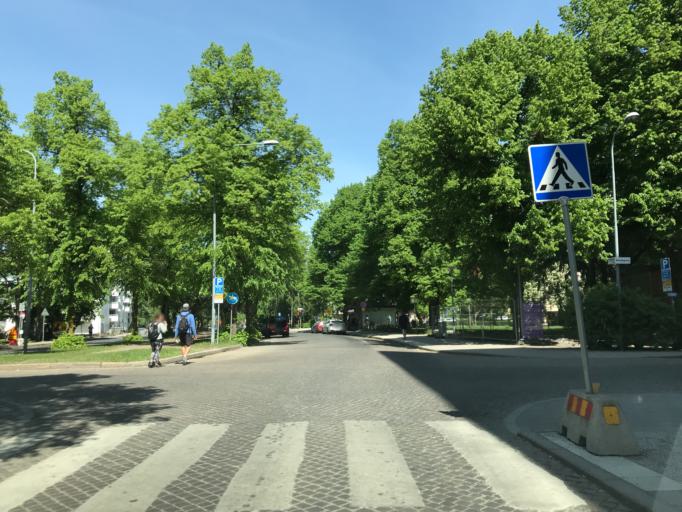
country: SE
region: Stockholm
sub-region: Stockholms Kommun
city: OEstermalm
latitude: 59.3443
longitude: 18.0931
